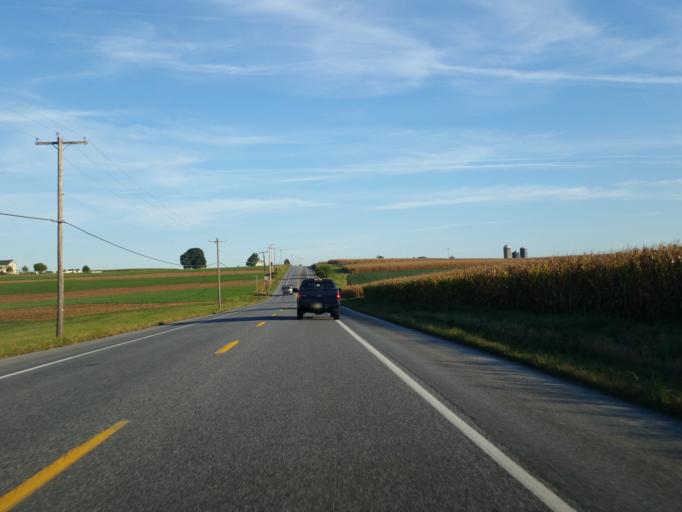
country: US
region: Pennsylvania
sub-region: Lancaster County
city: Quarryville
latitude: 39.8394
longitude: -76.2165
